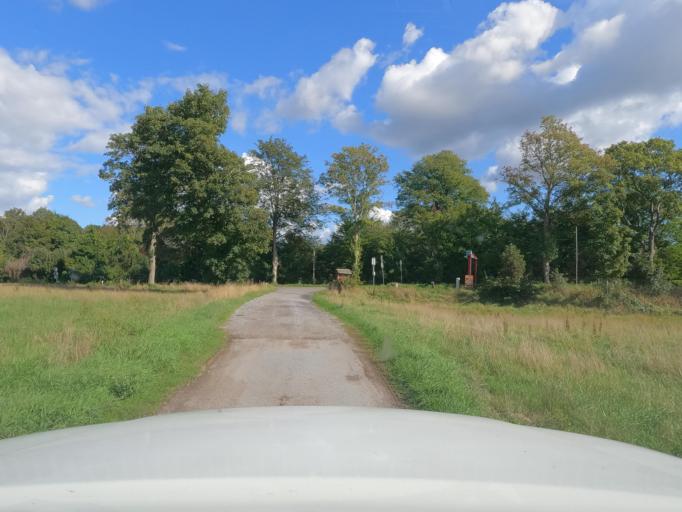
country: DE
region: North Rhine-Westphalia
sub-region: Regierungsbezirk Dusseldorf
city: Hunxe
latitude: 51.6563
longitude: 6.8104
